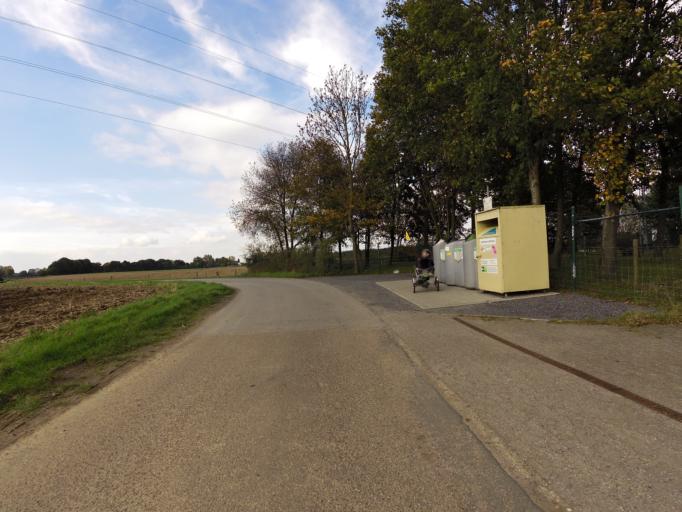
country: DE
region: North Rhine-Westphalia
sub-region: Regierungsbezirk Dusseldorf
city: Hamminkeln
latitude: 51.7775
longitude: 6.5619
